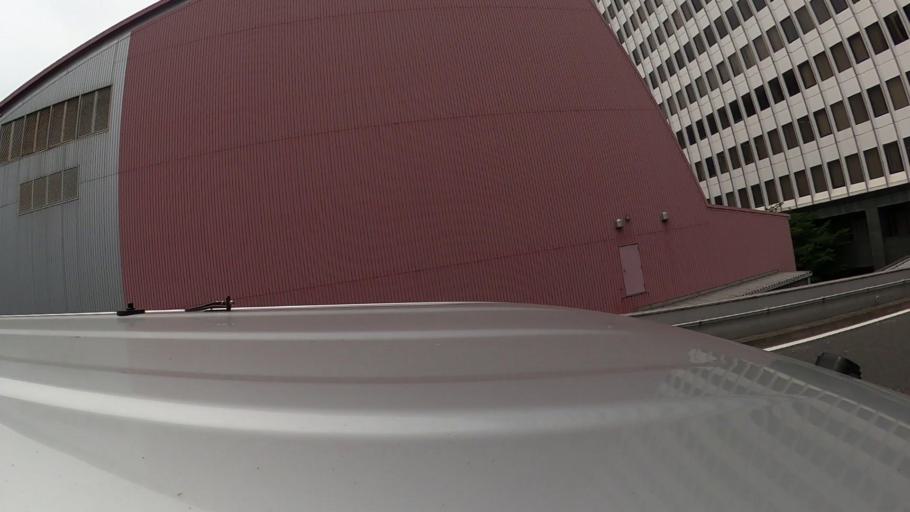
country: JP
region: Tokyo
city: Tokyo
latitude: 35.6758
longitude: 139.7655
